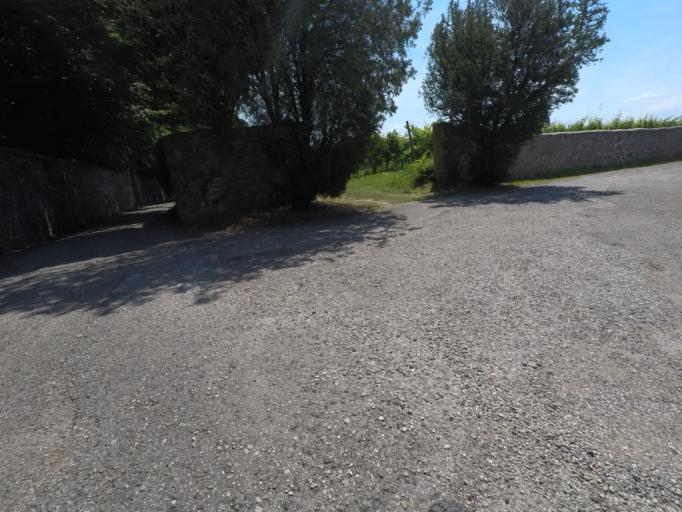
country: IT
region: Friuli Venezia Giulia
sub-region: Provincia di Udine
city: Tarcento
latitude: 46.1952
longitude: 13.2254
